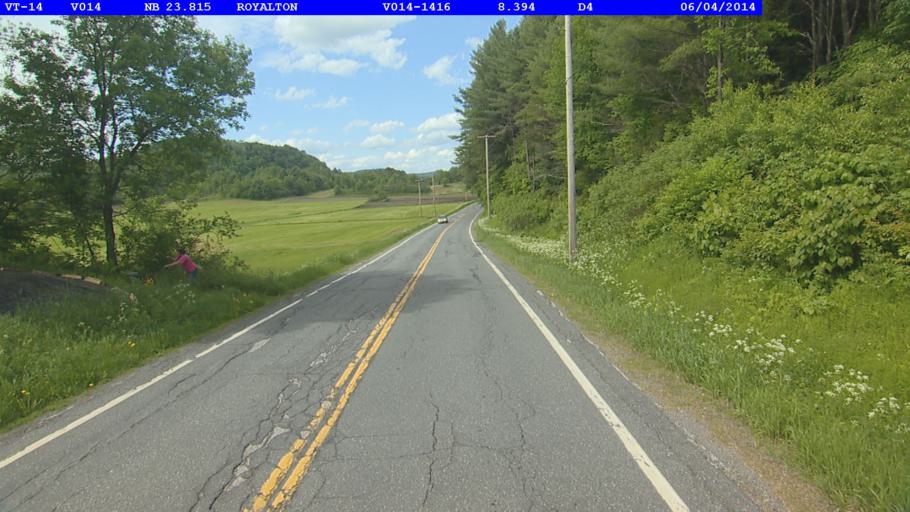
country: US
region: Vermont
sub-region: Orange County
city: Randolph
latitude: 43.8534
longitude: -72.5822
